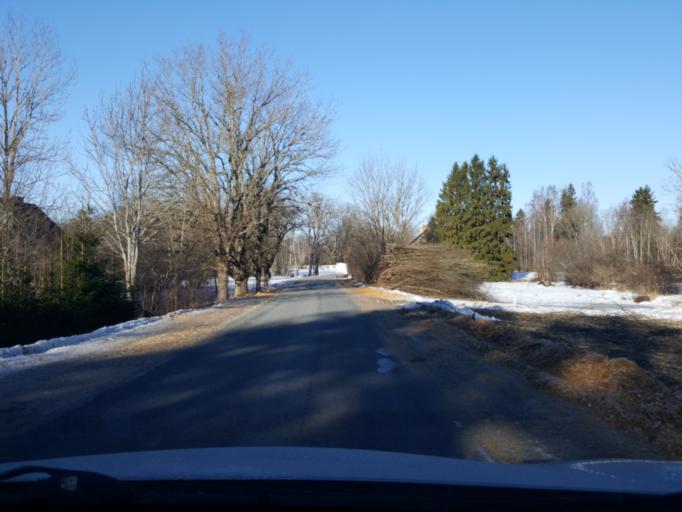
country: EE
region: Viljandimaa
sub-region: Viljandi linn
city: Viljandi
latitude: 58.4170
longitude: 25.5452
